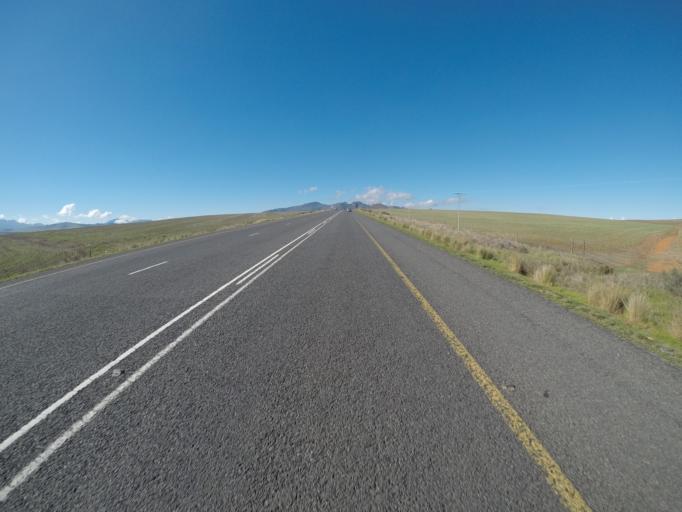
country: ZA
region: Western Cape
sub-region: Overberg District Municipality
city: Caledon
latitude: -34.2106
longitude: 19.3763
